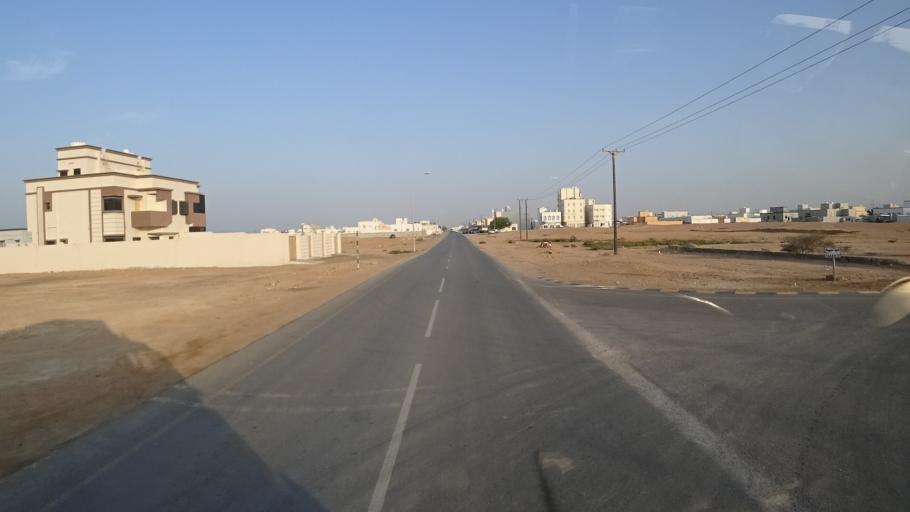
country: OM
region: Ash Sharqiyah
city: Sur
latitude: 22.6168
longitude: 59.4605
